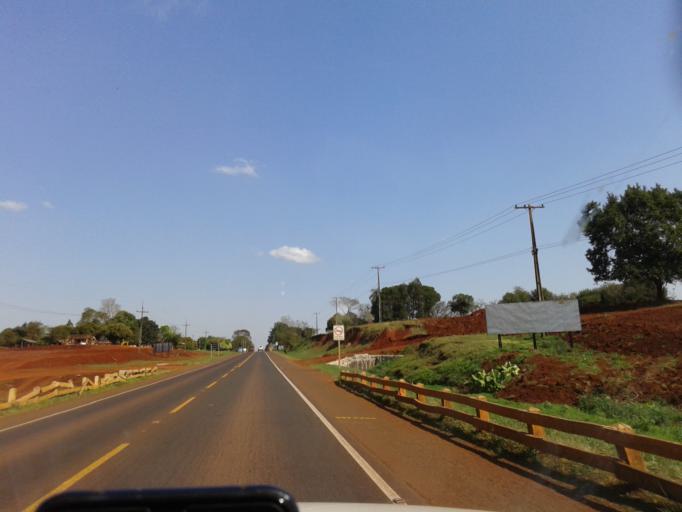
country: PY
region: Alto Parana
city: Santa Rita
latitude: -25.6582
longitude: -54.9897
